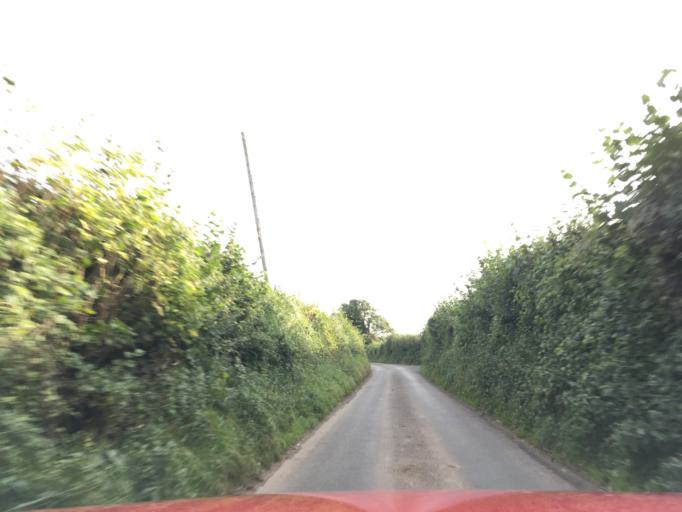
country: GB
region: England
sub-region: South Gloucestershire
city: Alveston
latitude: 51.5948
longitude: -2.5478
